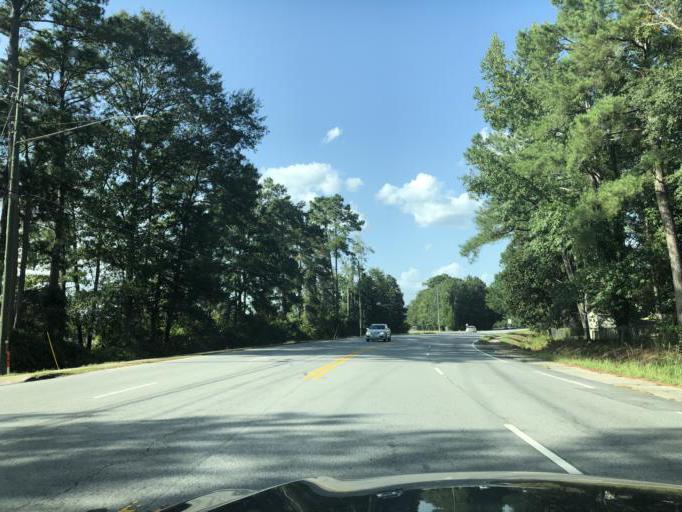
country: US
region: Georgia
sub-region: Muscogee County
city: Columbus
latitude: 32.4886
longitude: -84.8965
